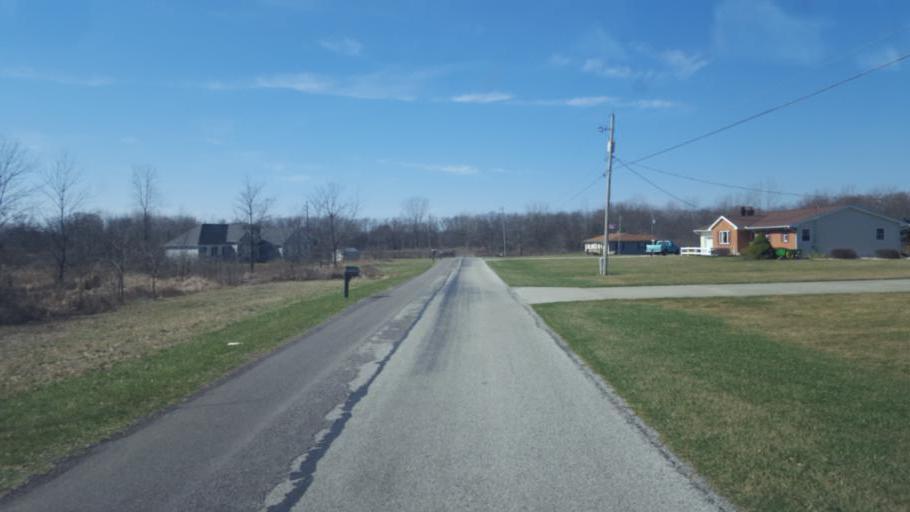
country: US
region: Ohio
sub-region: Marion County
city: Prospect
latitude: 40.4914
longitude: -83.1883
